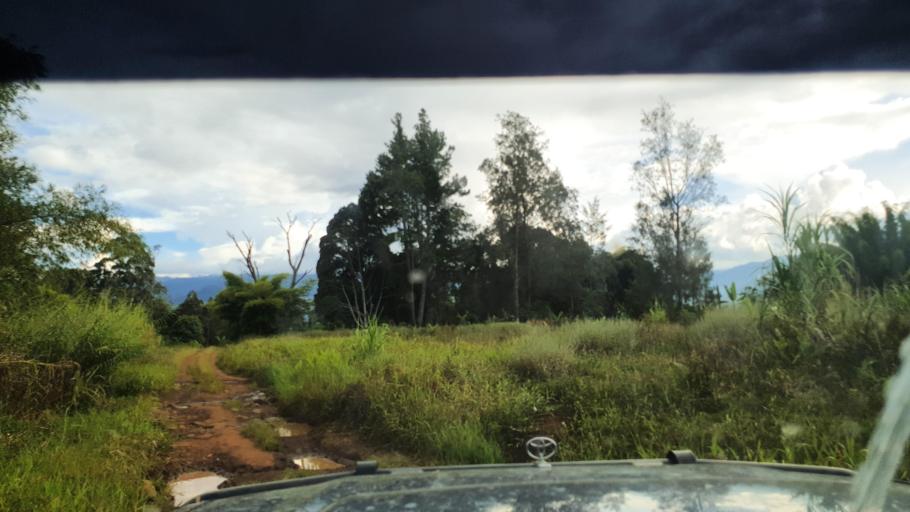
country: PG
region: Jiwaka
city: Minj
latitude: -5.9244
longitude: 144.8197
